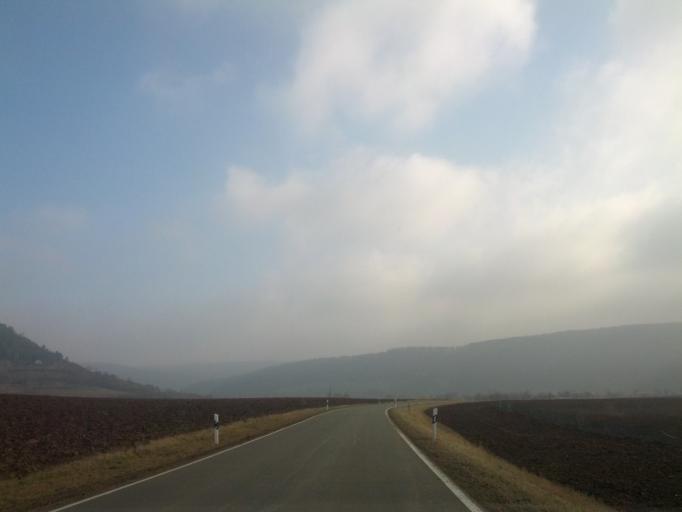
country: DE
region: Thuringia
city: Treffurt
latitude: 51.1232
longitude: 10.2580
